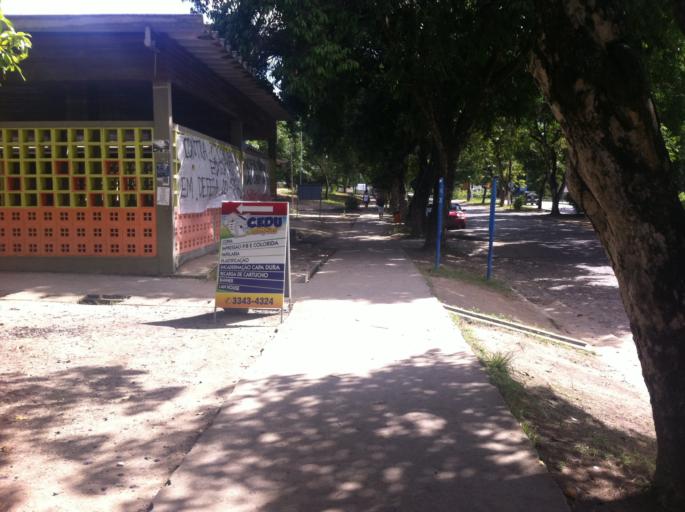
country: BR
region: Alagoas
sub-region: Satuba
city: Satuba
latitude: -9.5547
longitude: -35.7757
